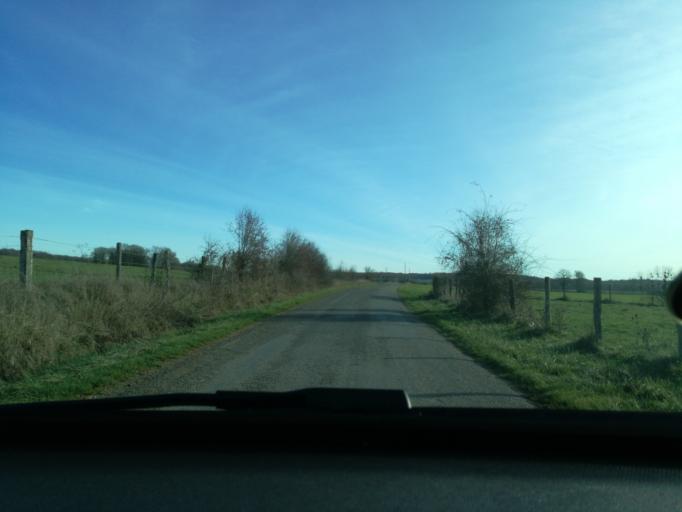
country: FR
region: Lorraine
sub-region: Departement de la Meuse
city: Revigny-sur-Ornain
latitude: 48.8198
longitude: 5.0568
